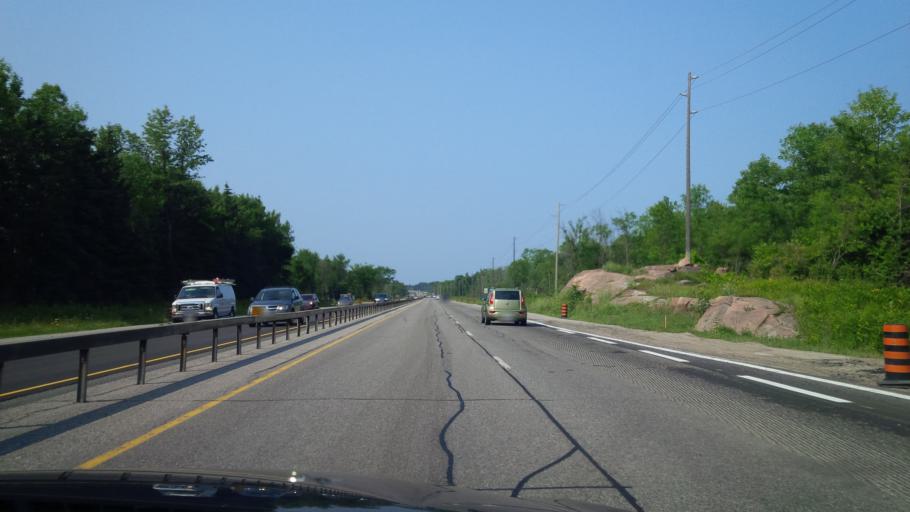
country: CA
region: Ontario
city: Orillia
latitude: 44.7394
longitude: -79.3521
